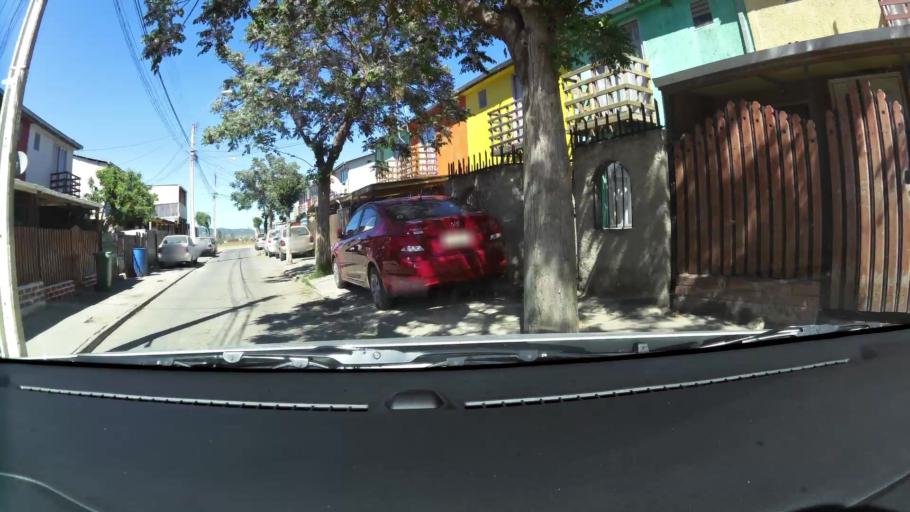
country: CL
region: Valparaiso
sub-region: Provincia de Marga Marga
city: Quilpue
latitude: -33.3056
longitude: -71.4137
